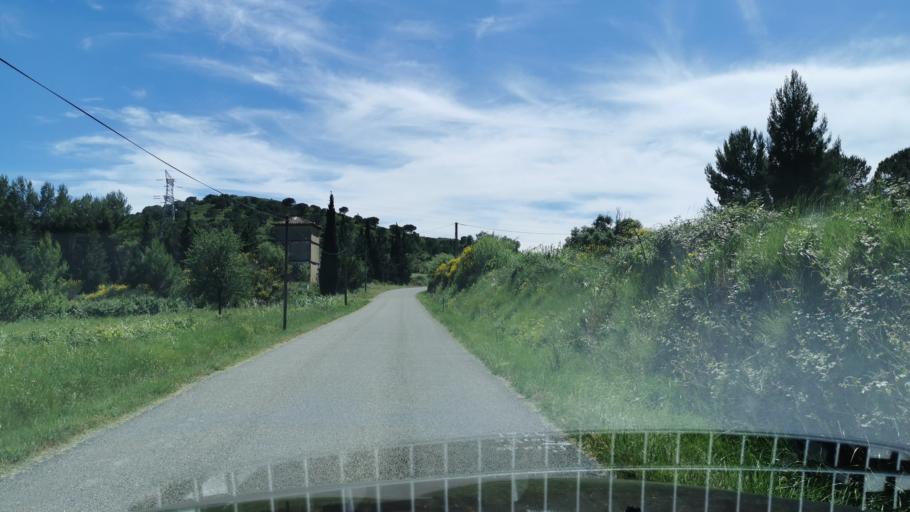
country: FR
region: Languedoc-Roussillon
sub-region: Departement de l'Aude
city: Nevian
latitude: 43.2035
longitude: 2.9034
